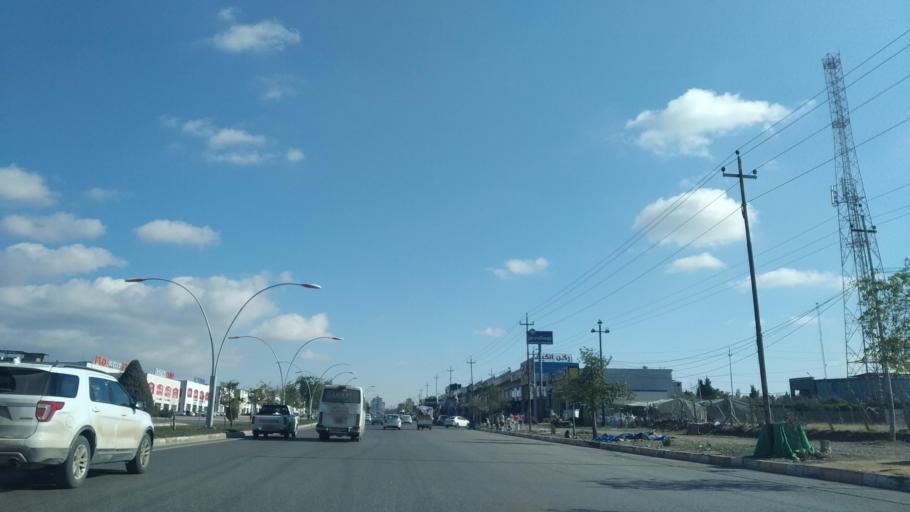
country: IQ
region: Arbil
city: Erbil
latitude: 36.2007
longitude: 44.0934
